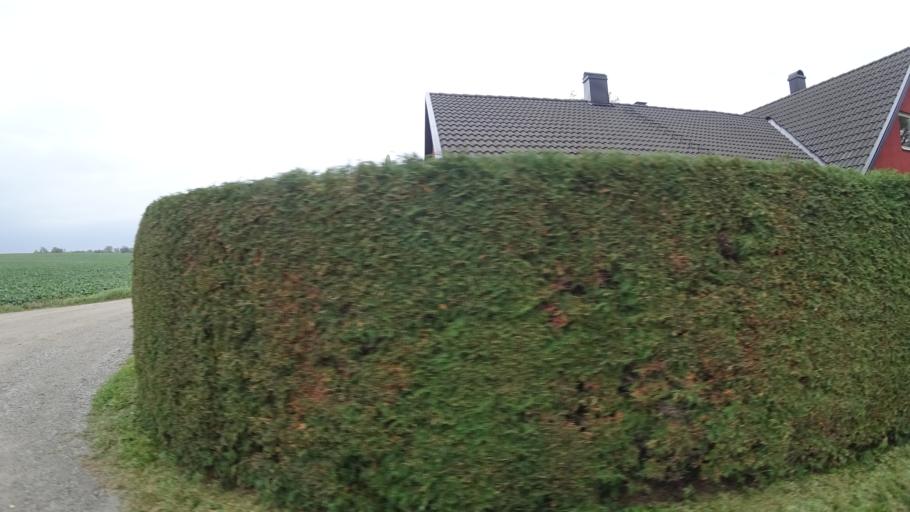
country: SE
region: Skane
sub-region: Kavlinge Kommun
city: Kaevlinge
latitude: 55.8002
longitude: 13.1411
